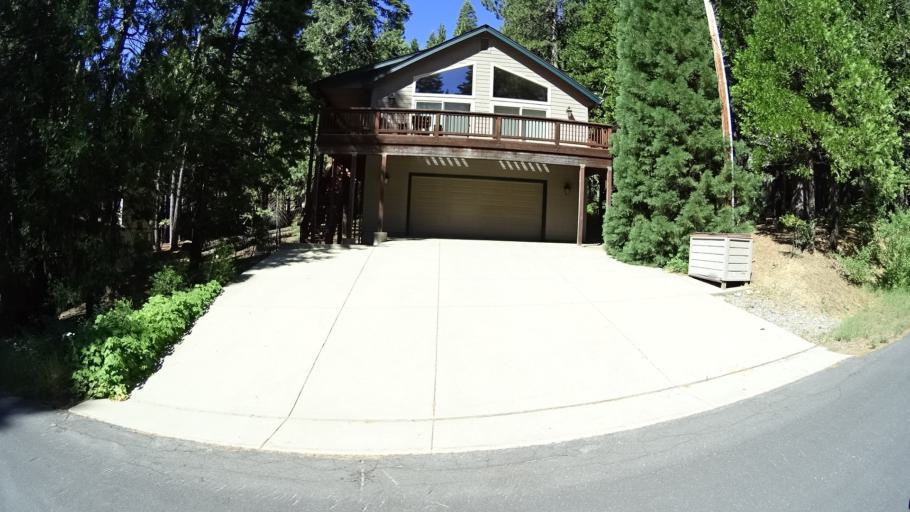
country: US
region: California
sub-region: Calaveras County
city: Arnold
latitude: 38.2878
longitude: -120.2730
